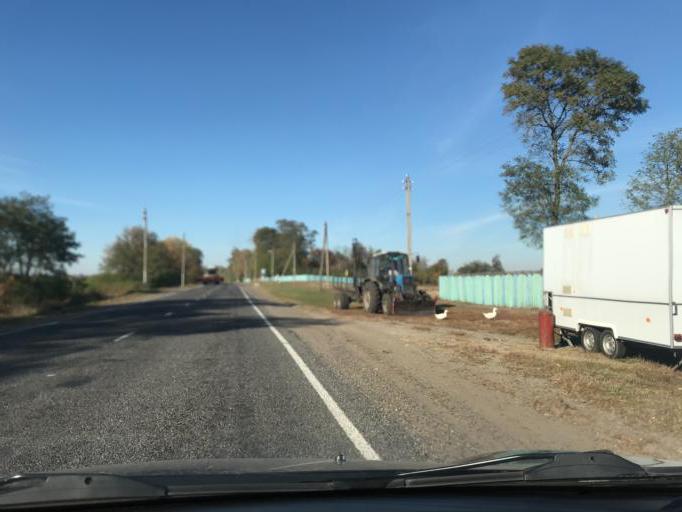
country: BY
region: Gomel
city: Brahin
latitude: 51.6706
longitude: 30.3849
